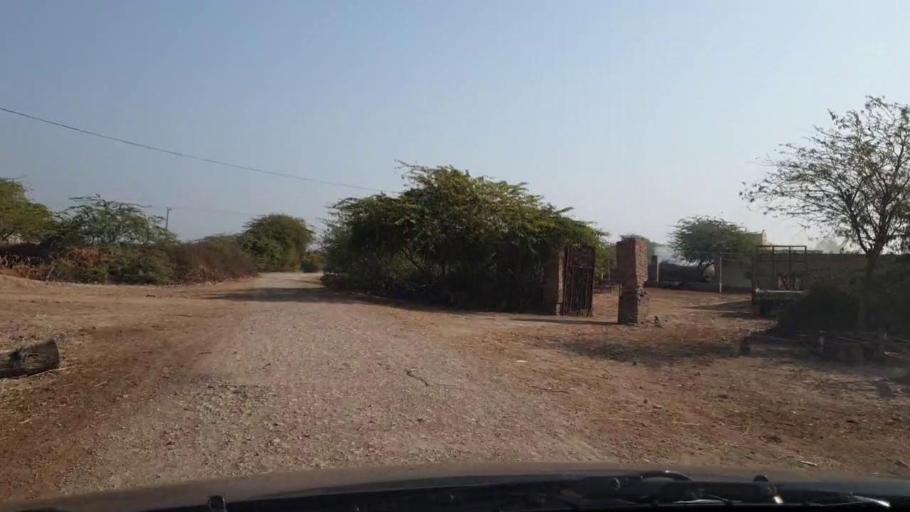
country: PK
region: Sindh
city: Sanghar
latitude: 25.9644
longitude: 69.0136
